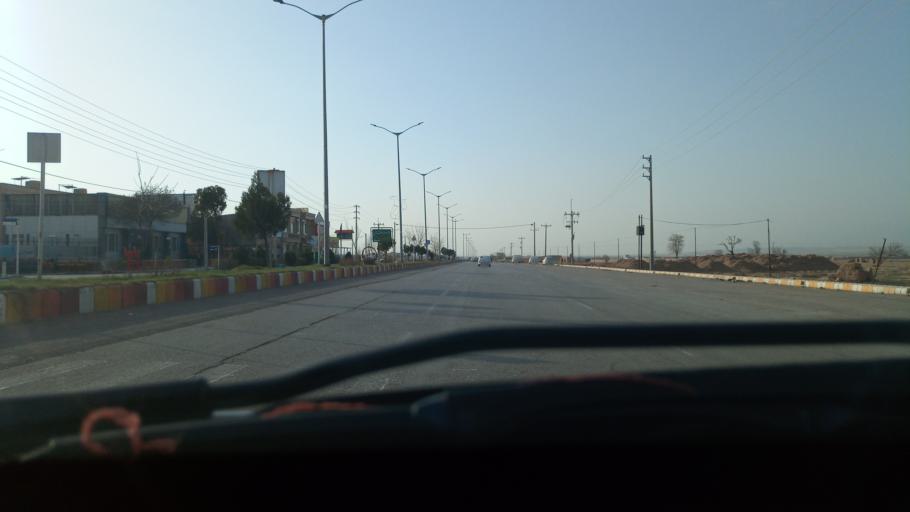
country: IR
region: Khorasan-e Shomali
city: Faruj
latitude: 37.2354
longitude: 58.2151
